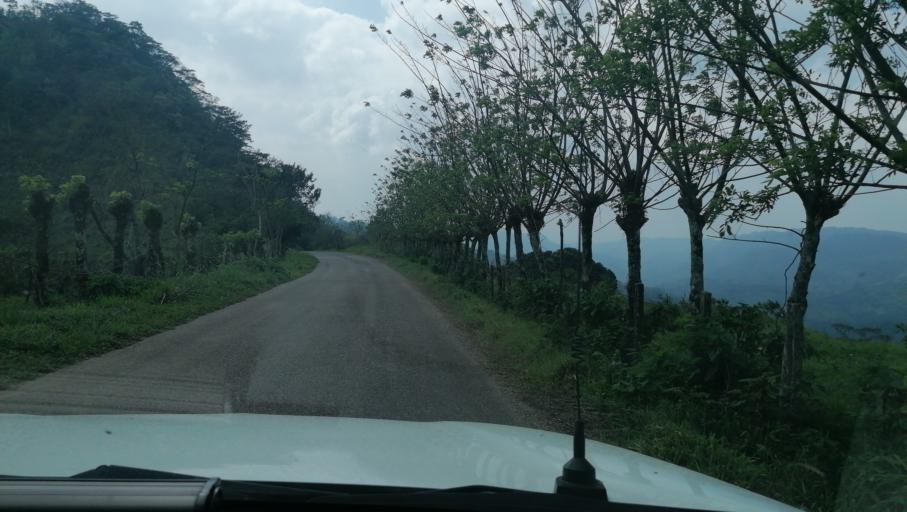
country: MX
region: Chiapas
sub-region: Francisco Leon
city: San Miguel la Sardina
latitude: 17.2375
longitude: -93.3212
